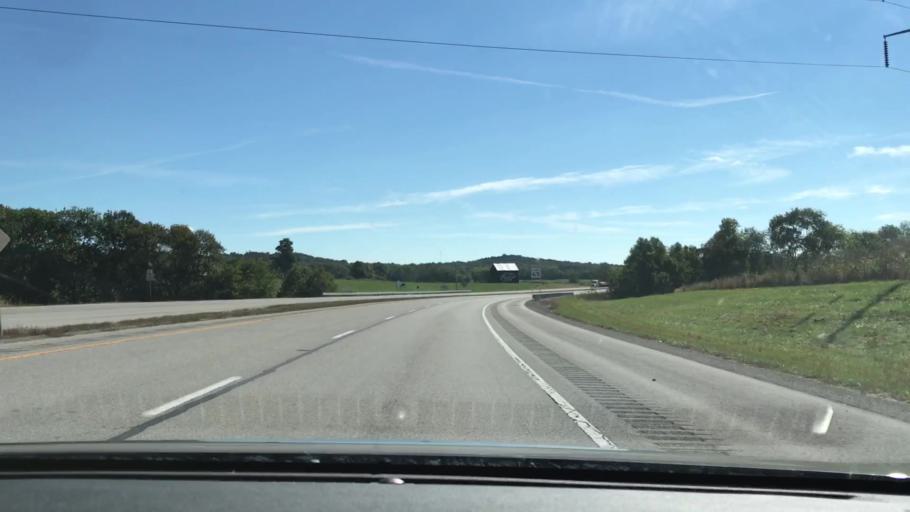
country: US
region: Kentucky
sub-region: Todd County
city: Elkton
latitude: 36.8239
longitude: -87.1501
